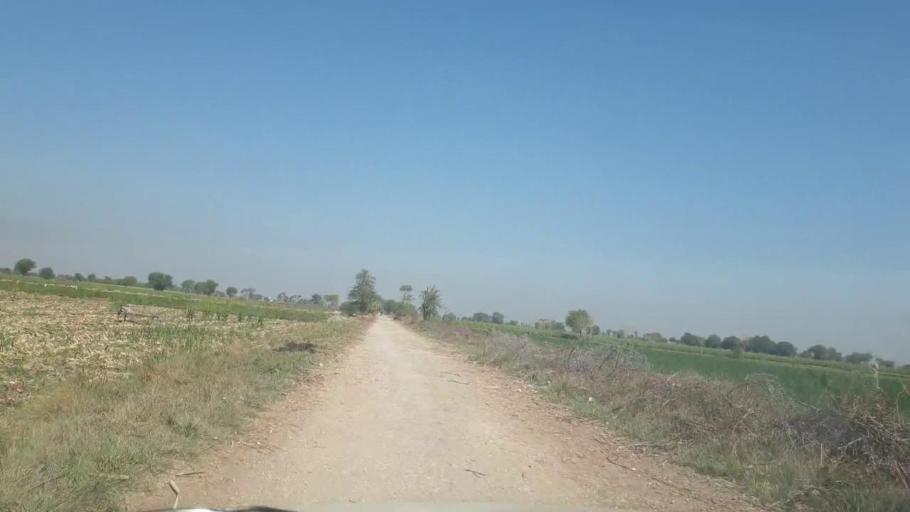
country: PK
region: Sindh
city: Mirpur Khas
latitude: 25.5469
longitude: 69.1965
